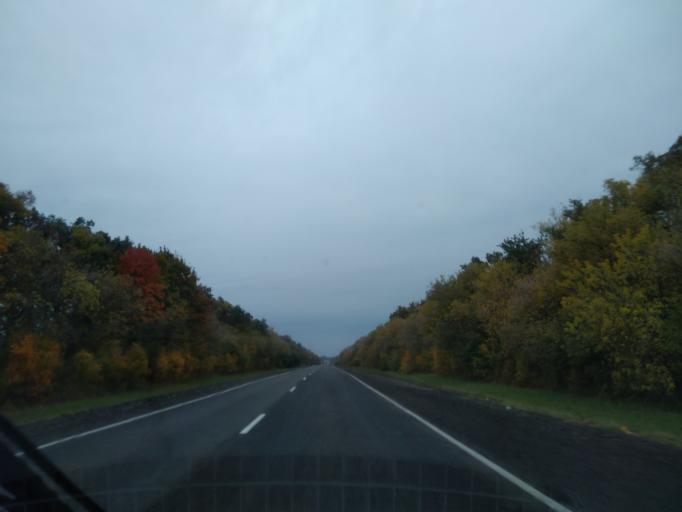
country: RU
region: Lipetsk
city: Zadonsk
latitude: 52.4653
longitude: 38.7724
